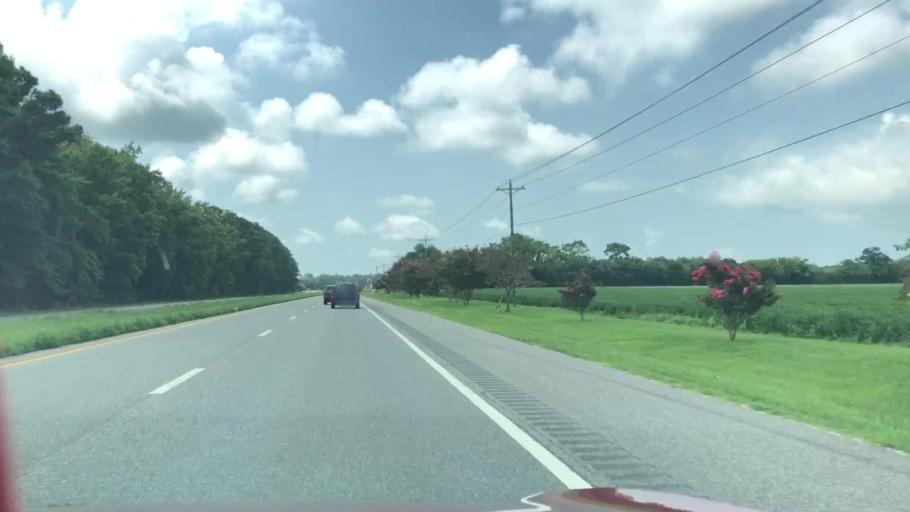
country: US
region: Virginia
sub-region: Northampton County
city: Eastville
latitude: 37.3094
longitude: -75.9625
